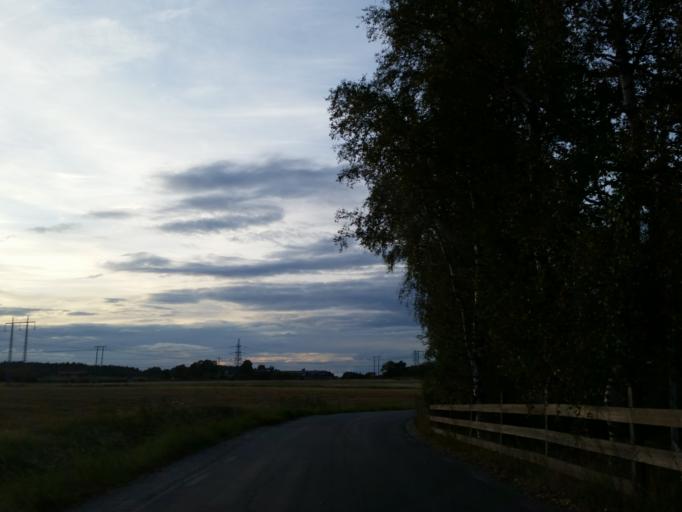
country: SE
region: Stockholm
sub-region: Sigtuna Kommun
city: Marsta
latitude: 59.6337
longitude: 17.8811
